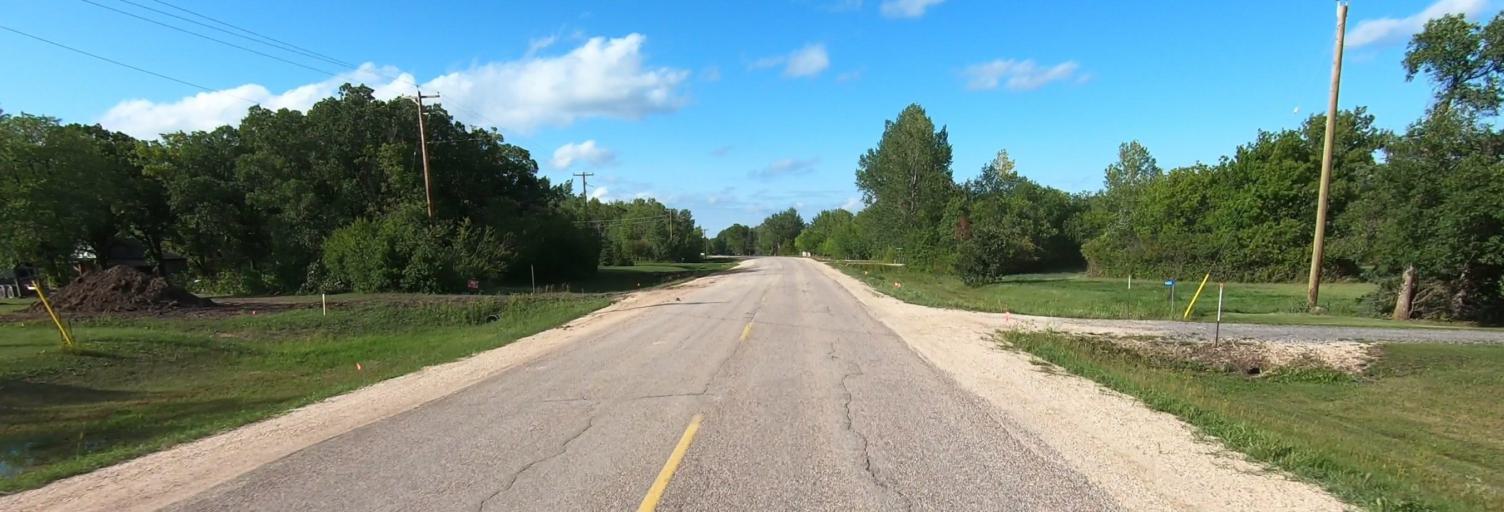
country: CA
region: Manitoba
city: Selkirk
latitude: 50.2165
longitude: -96.8398
